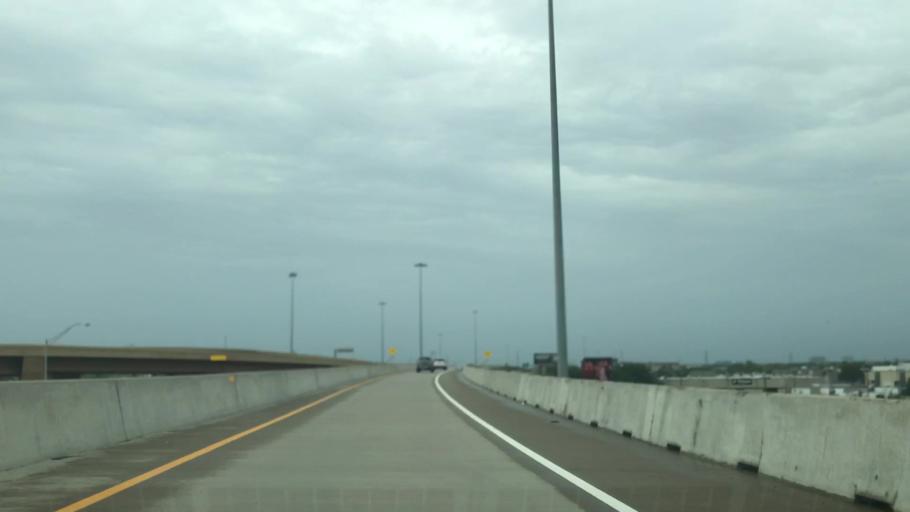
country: US
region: Texas
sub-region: Dallas County
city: Farmers Branch
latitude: 32.8690
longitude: -96.8968
